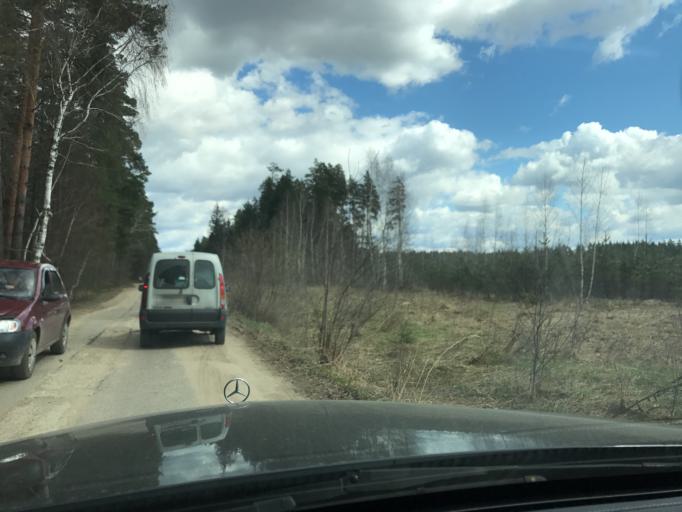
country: RU
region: Vladimir
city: Pokrov
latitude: 55.8730
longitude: 39.2407
